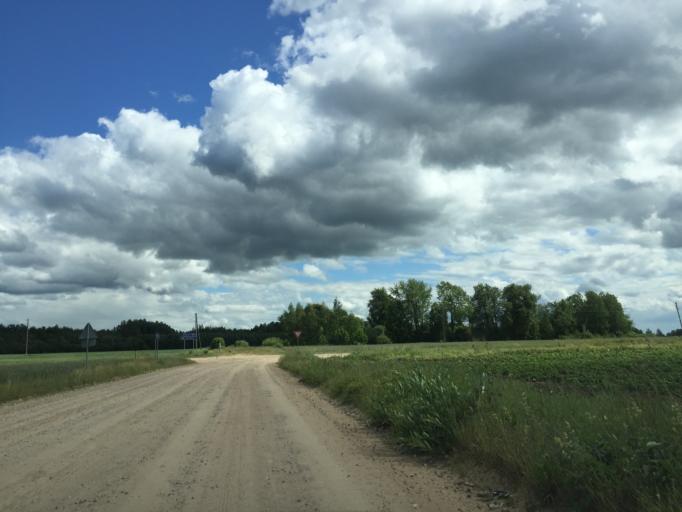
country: LV
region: Lecava
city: Iecava
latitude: 56.5003
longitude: 24.3603
